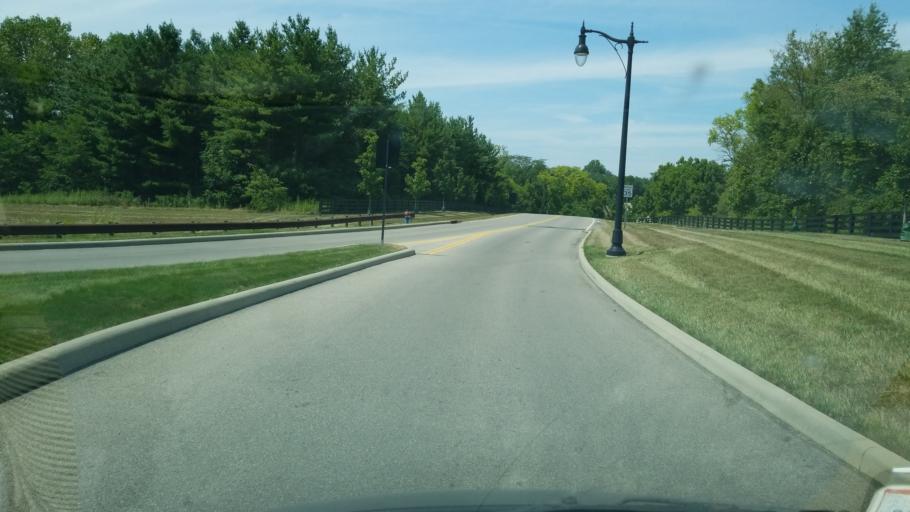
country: US
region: Ohio
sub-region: Union County
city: New California
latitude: 40.1737
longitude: -83.1870
